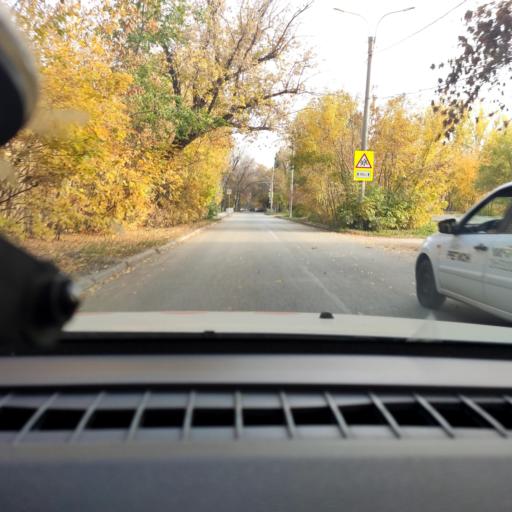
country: RU
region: Samara
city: Samara
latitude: 53.1195
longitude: 50.0773
